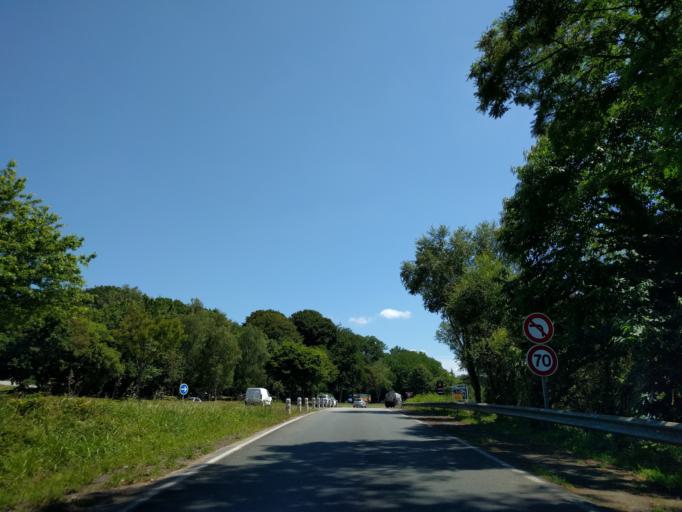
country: FR
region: Brittany
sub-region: Departement du Finistere
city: Quimper
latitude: 47.9801
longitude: -4.1020
